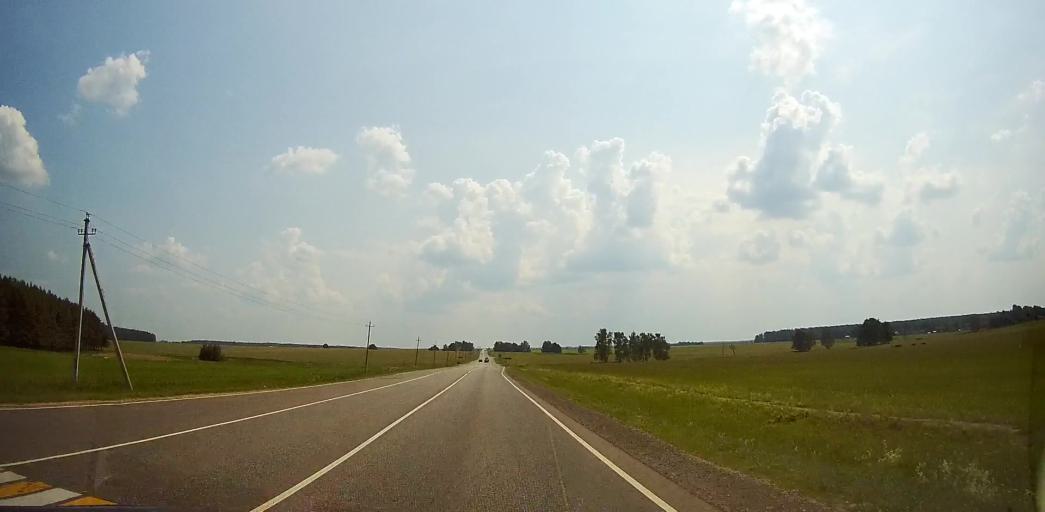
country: RU
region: Moskovskaya
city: Malino
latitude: 55.0494
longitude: 38.1468
